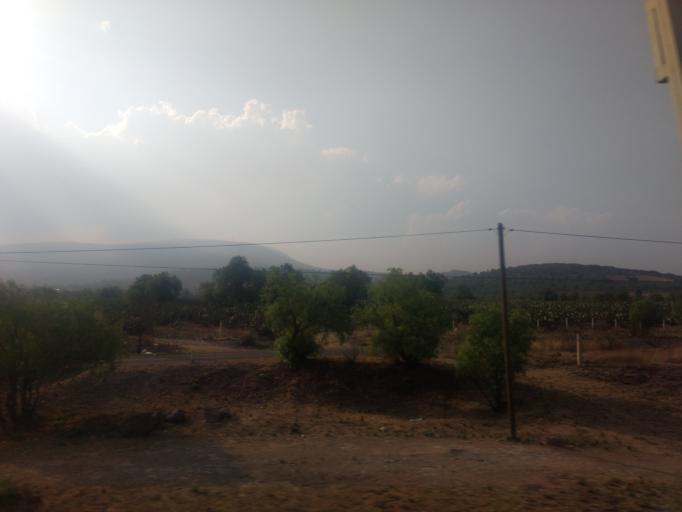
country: MX
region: Mexico
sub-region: Axapusco
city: Colonia los Remedios
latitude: 19.7312
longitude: -98.7767
